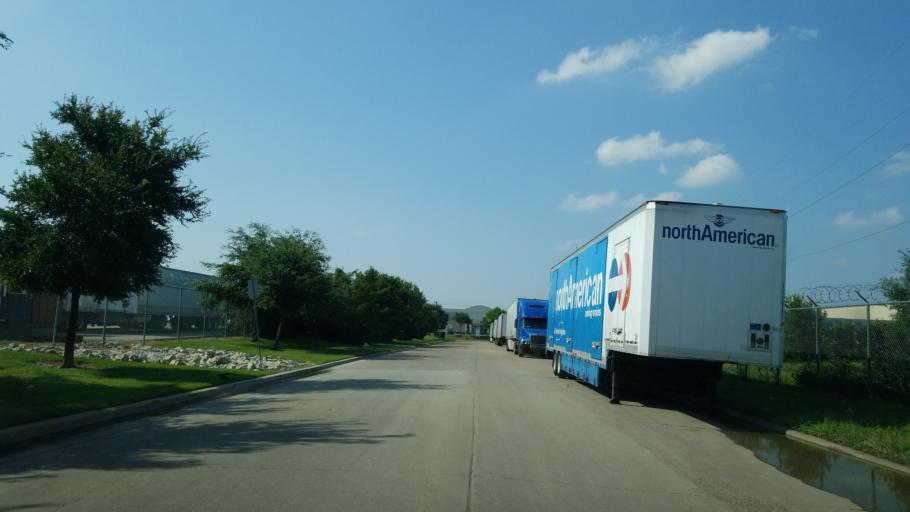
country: US
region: Texas
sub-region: Dallas County
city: Farmers Branch
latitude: 32.8721
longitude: -96.9051
